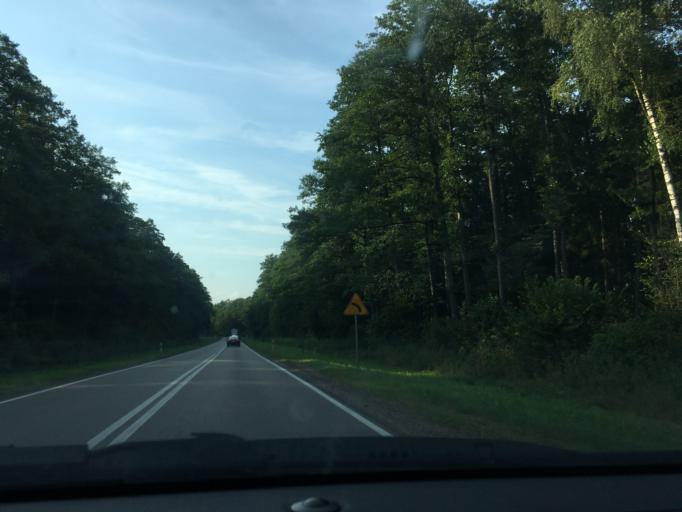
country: PL
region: Podlasie
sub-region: Powiat moniecki
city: Knyszyn
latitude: 53.2729
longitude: 22.9621
